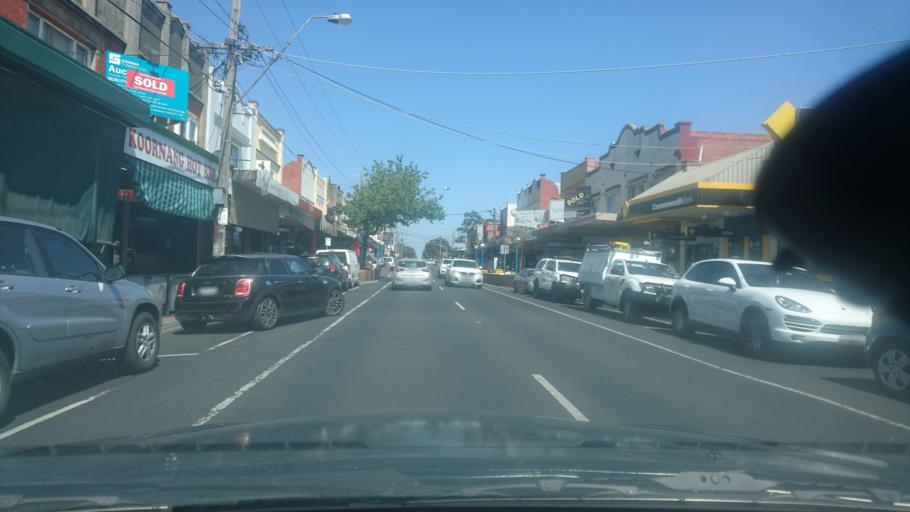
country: AU
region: Victoria
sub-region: Glen Eira
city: Carnegie
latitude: -37.8880
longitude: 145.0573
